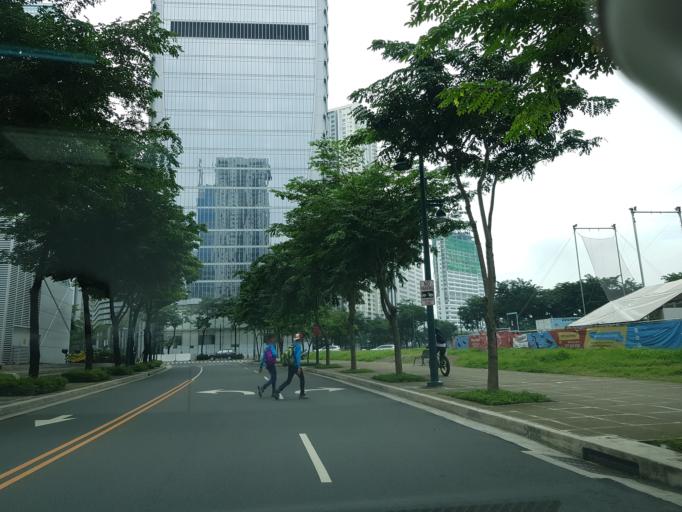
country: PH
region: Metro Manila
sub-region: Makati City
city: Makati City
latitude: 14.5475
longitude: 121.0493
